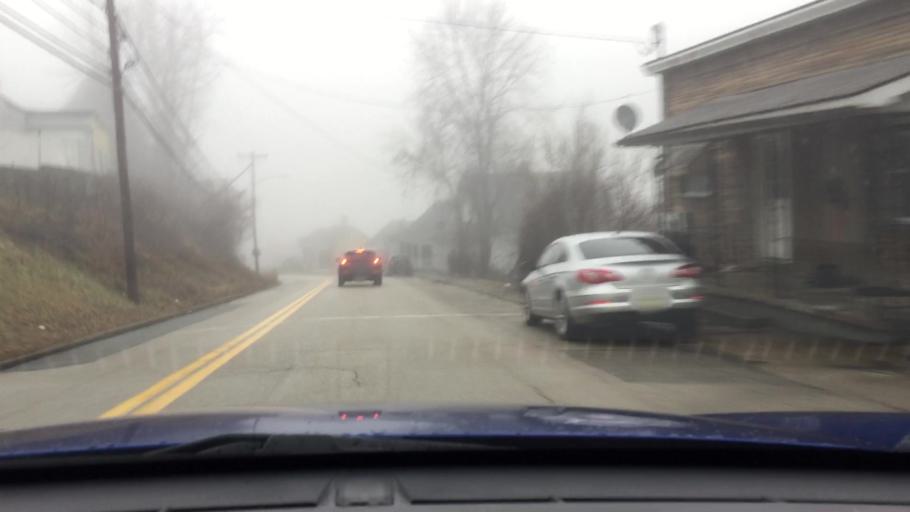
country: US
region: Pennsylvania
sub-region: Washington County
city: Canonsburg
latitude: 40.2511
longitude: -80.1845
